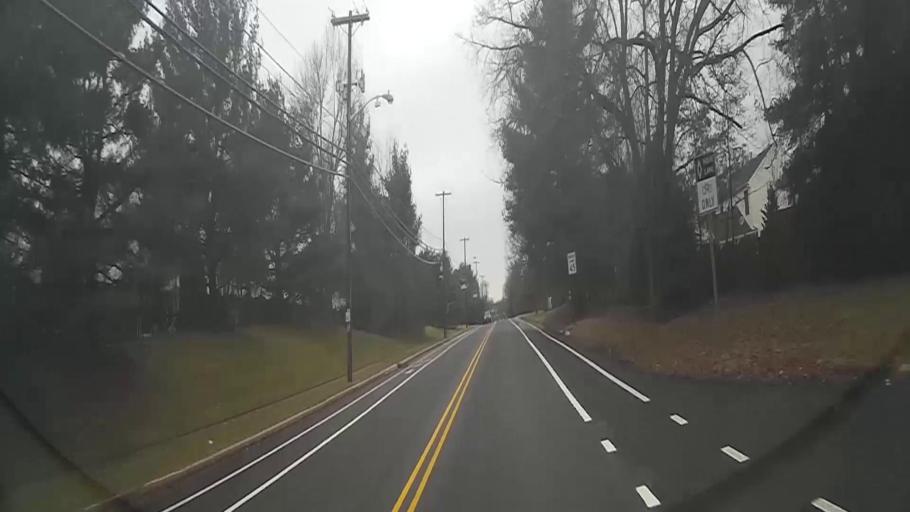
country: US
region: New Jersey
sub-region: Burlington County
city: Marlton
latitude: 39.8634
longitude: -74.9361
